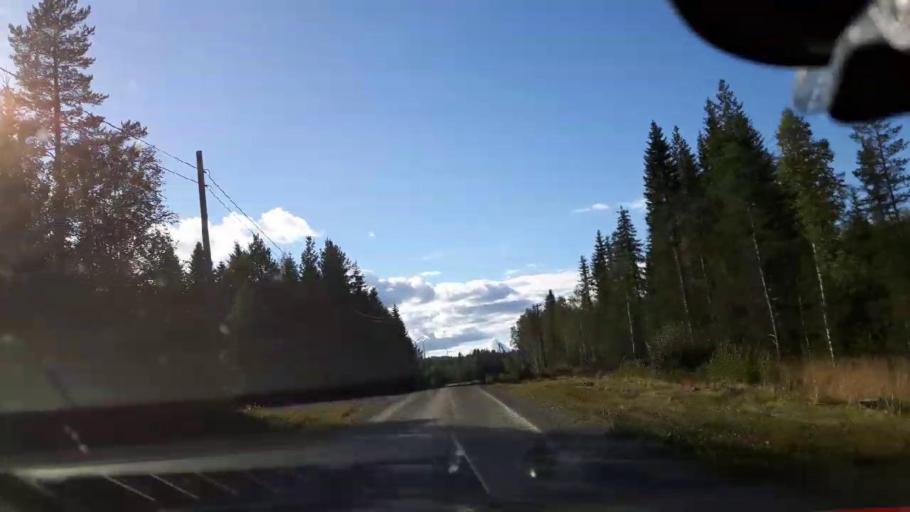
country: SE
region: Jaemtland
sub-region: Ragunda Kommun
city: Hammarstrand
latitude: 63.4893
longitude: 16.0633
